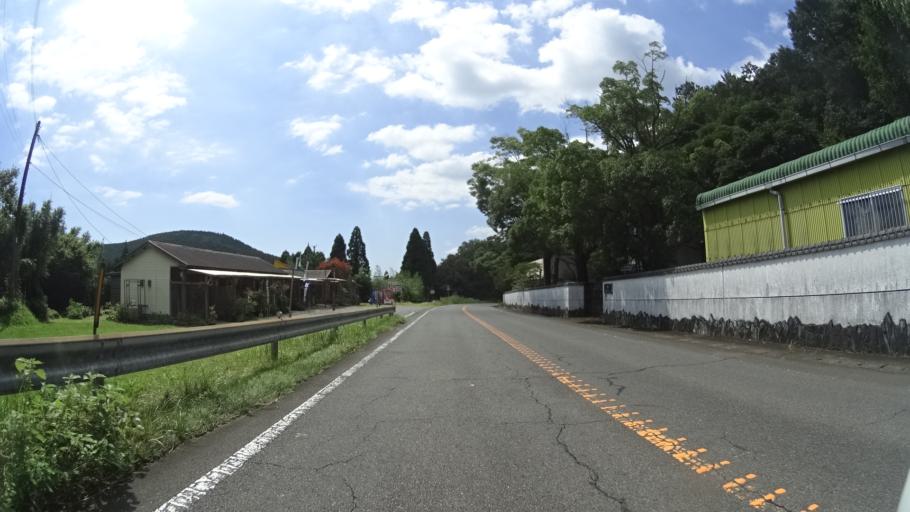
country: JP
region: Kagoshima
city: Kokubu-matsuki
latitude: 31.8751
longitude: 130.8000
